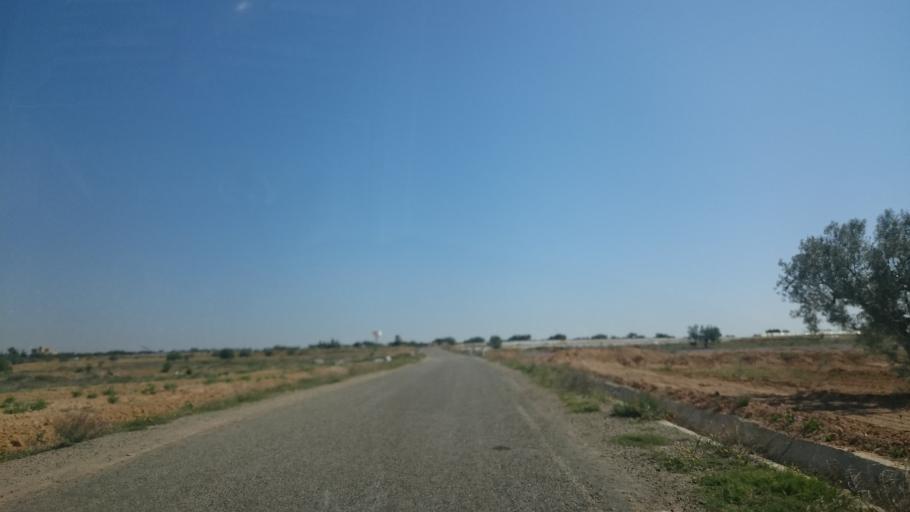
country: TN
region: Safaqis
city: Sfax
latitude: 34.7762
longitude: 10.5136
